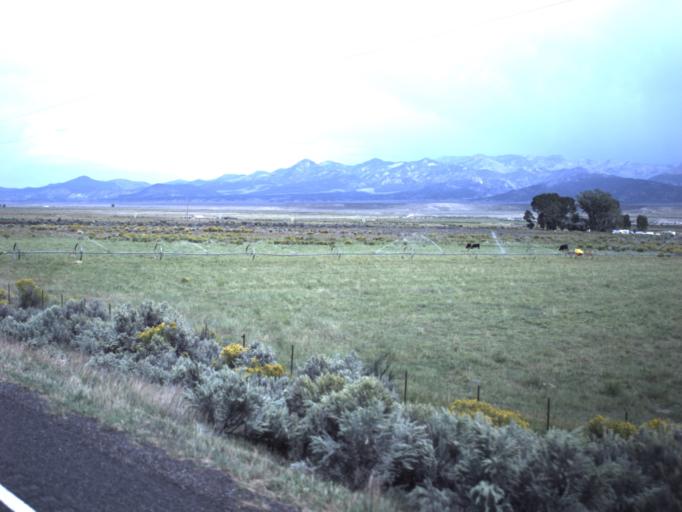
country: US
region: Utah
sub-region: Garfield County
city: Panguitch
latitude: 37.9139
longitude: -112.4281
